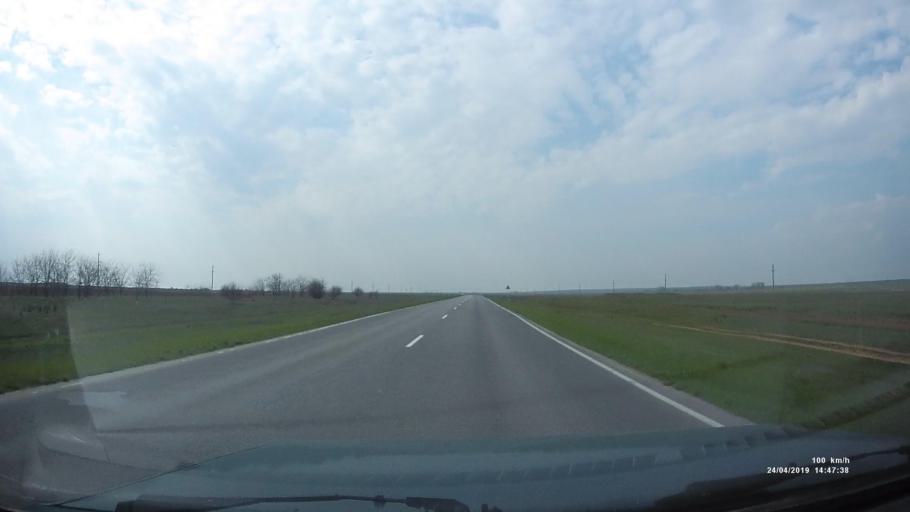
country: RU
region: Rostov
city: Remontnoye
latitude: 46.4934
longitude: 43.7697
